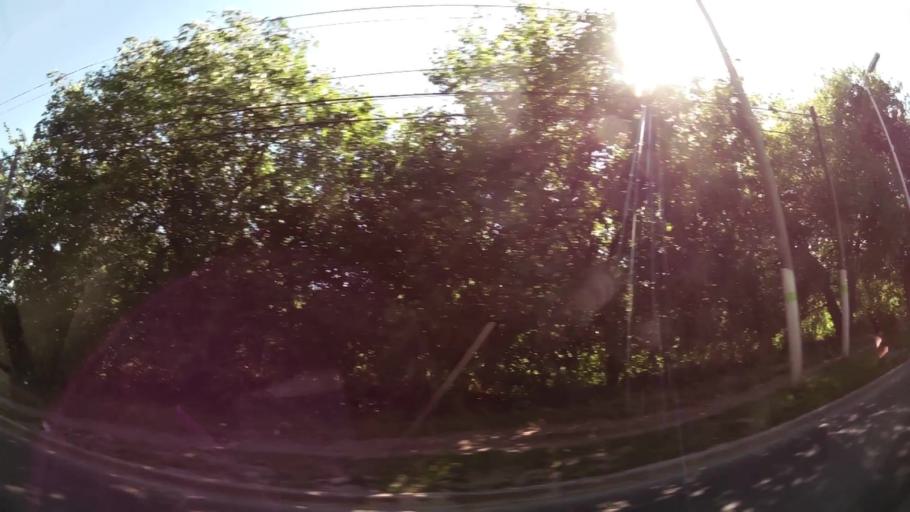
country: AR
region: Buenos Aires
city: Santa Catalina - Dique Lujan
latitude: -34.4721
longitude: -58.7074
